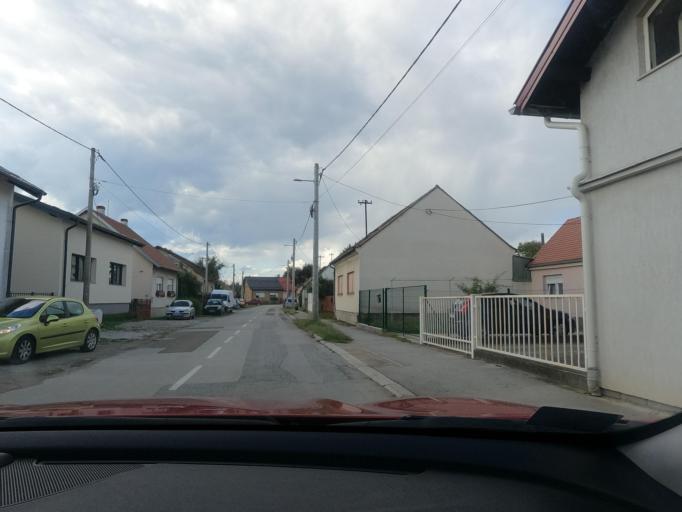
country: HR
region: Sisacko-Moslavacka
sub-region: Grad Sisak
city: Sisak
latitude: 45.4831
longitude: 16.3870
